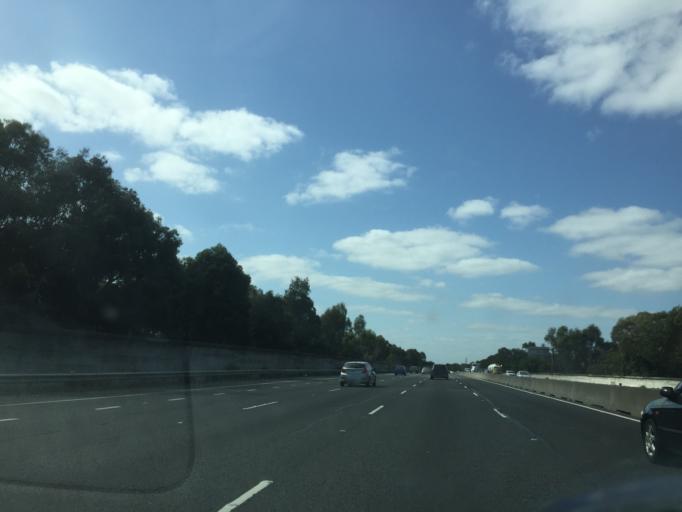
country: AU
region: New South Wales
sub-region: Holroyd
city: Merrylands
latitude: -33.8210
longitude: 150.9844
